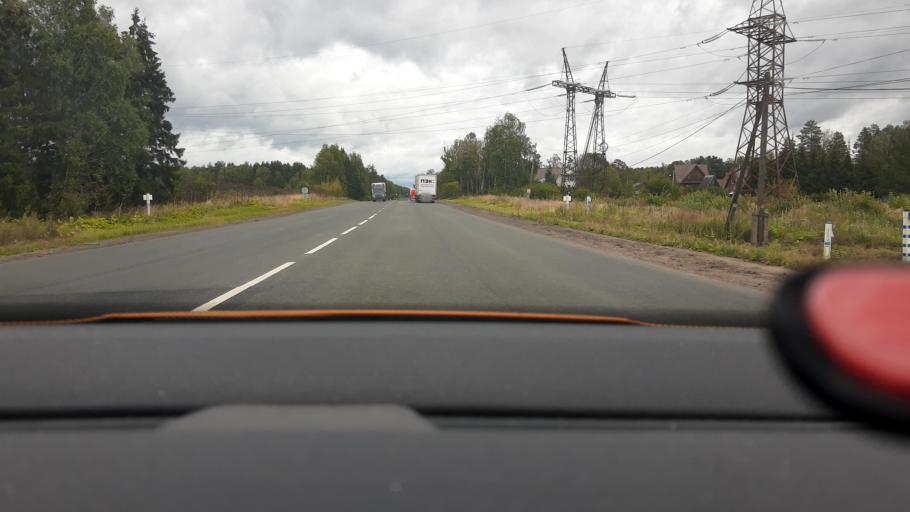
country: RU
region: Moskovskaya
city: Lesnoy
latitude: 56.0537
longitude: 37.9980
